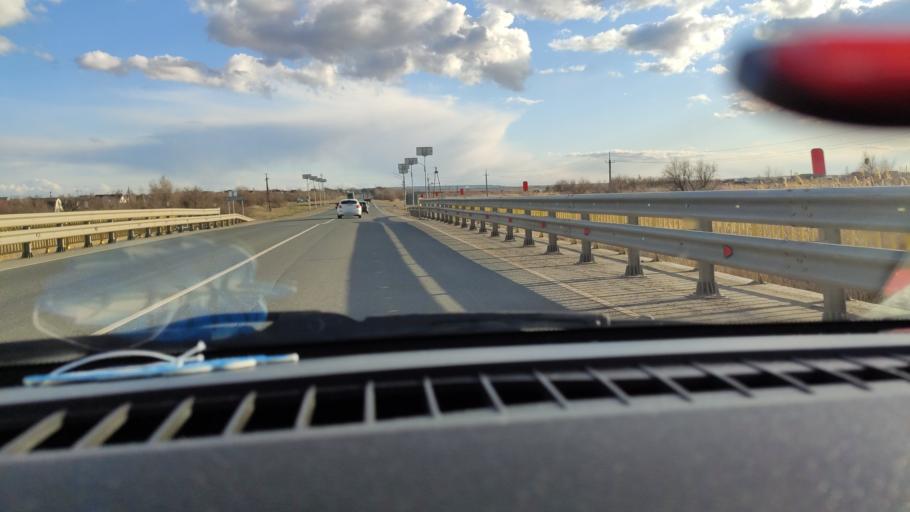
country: RU
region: Saratov
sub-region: Saratovskiy Rayon
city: Saratov
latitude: 51.6896
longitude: 46.0052
